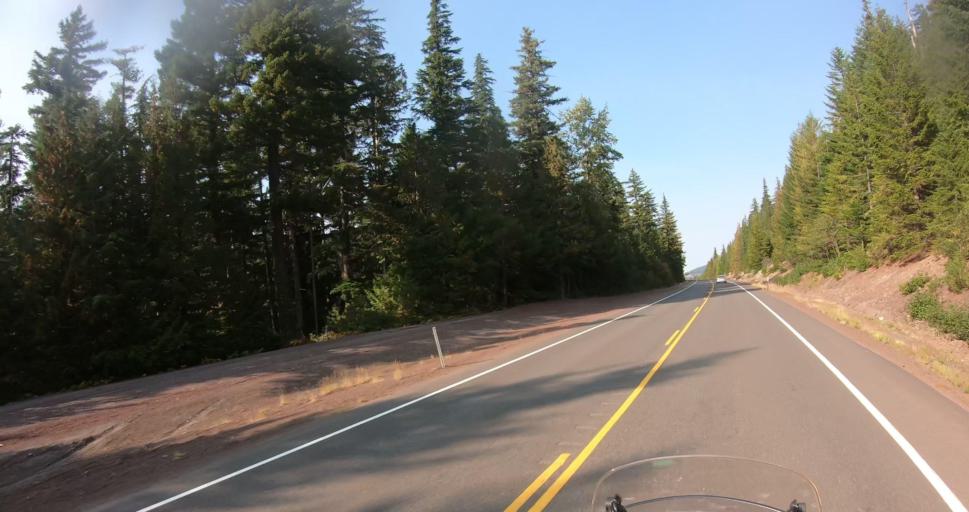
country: US
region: Oregon
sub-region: Hood River County
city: Odell
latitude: 45.3449
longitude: -121.5684
